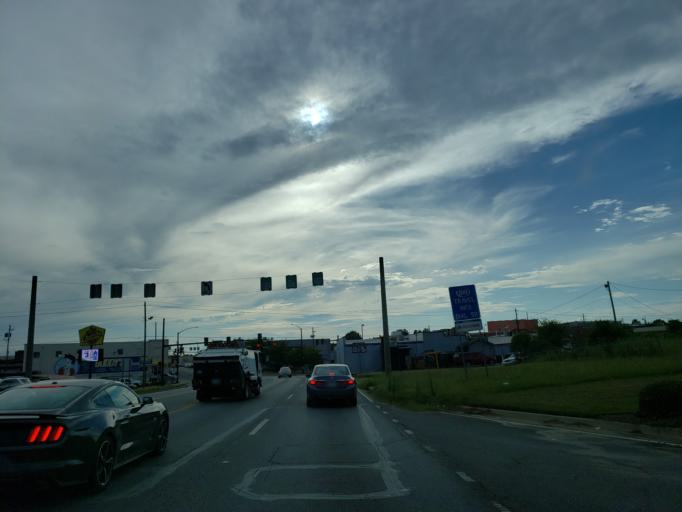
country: US
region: Georgia
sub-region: Tift County
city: Tifton
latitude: 31.4508
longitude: -83.5067
